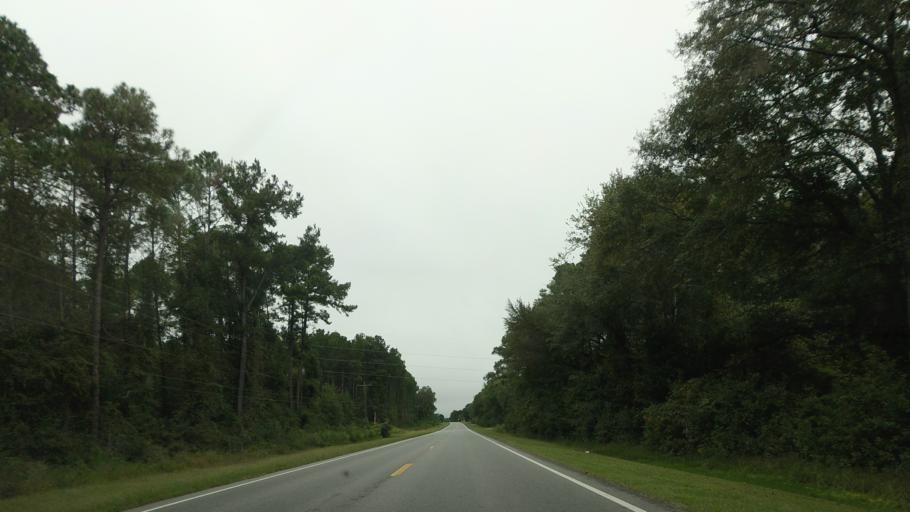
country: US
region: Georgia
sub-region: Berrien County
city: Nashville
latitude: 31.2267
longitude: -83.2475
